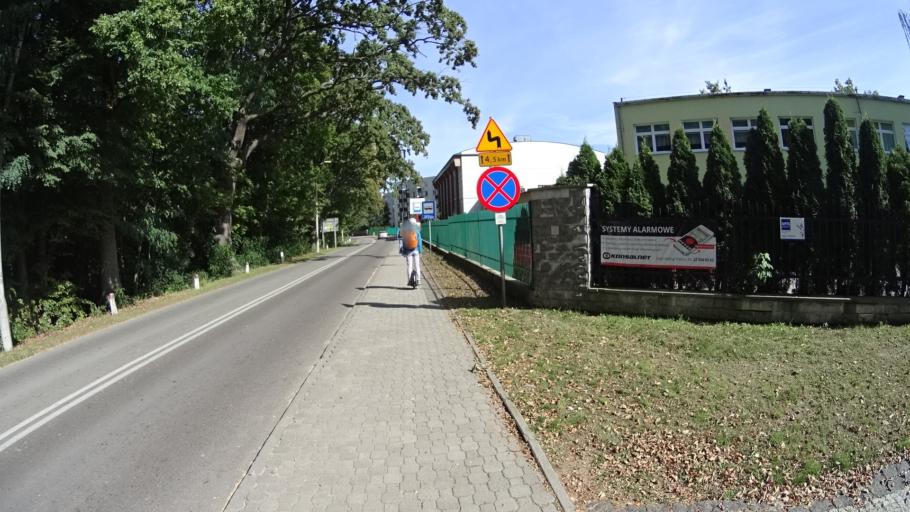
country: PL
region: Masovian Voivodeship
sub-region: Powiat legionowski
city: Bialobrzegi
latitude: 52.4422
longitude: 21.0532
